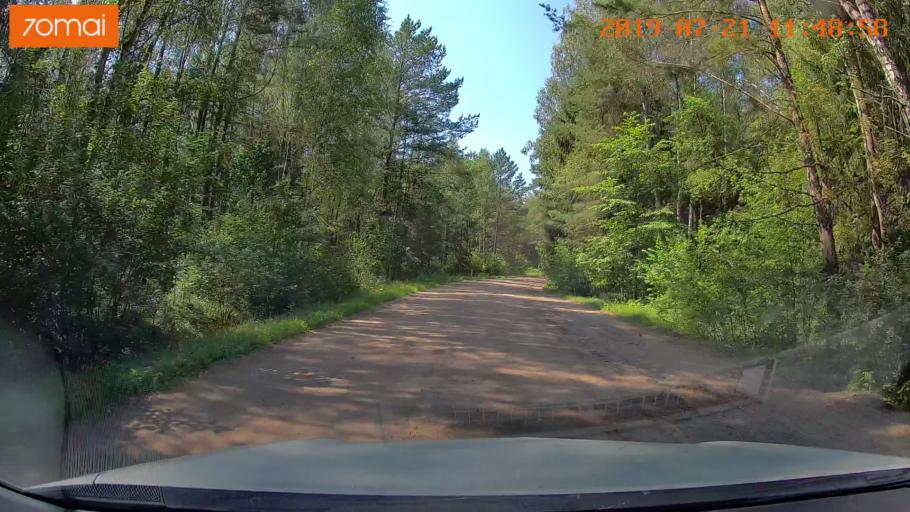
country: BY
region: Grodnenskaya
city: Lyubcha
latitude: 53.8945
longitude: 26.0439
